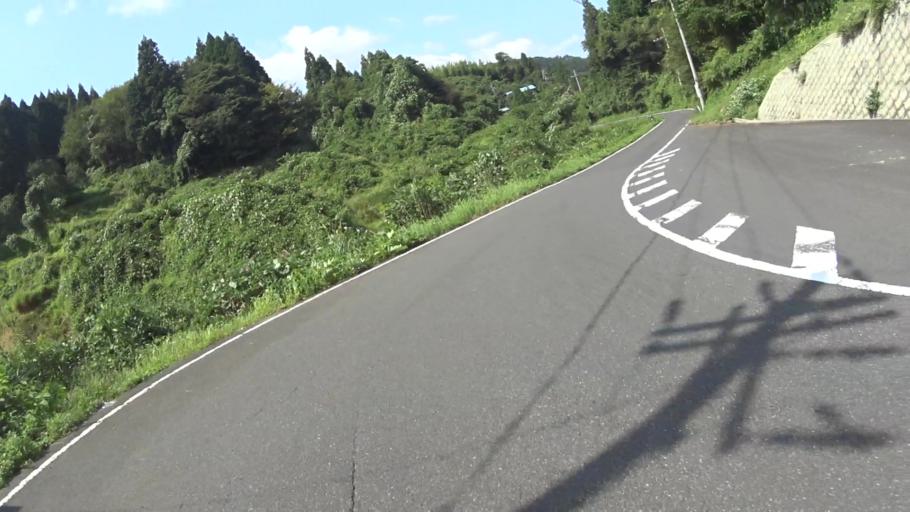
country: JP
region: Kyoto
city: Miyazu
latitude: 35.6859
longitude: 135.2574
